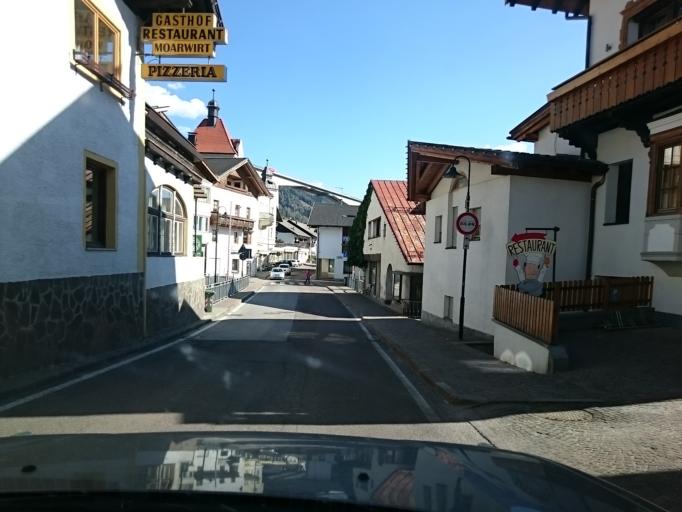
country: IT
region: Trentino-Alto Adige
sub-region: Bolzano
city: Brennero - Brenner
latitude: 46.9378
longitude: 11.4446
